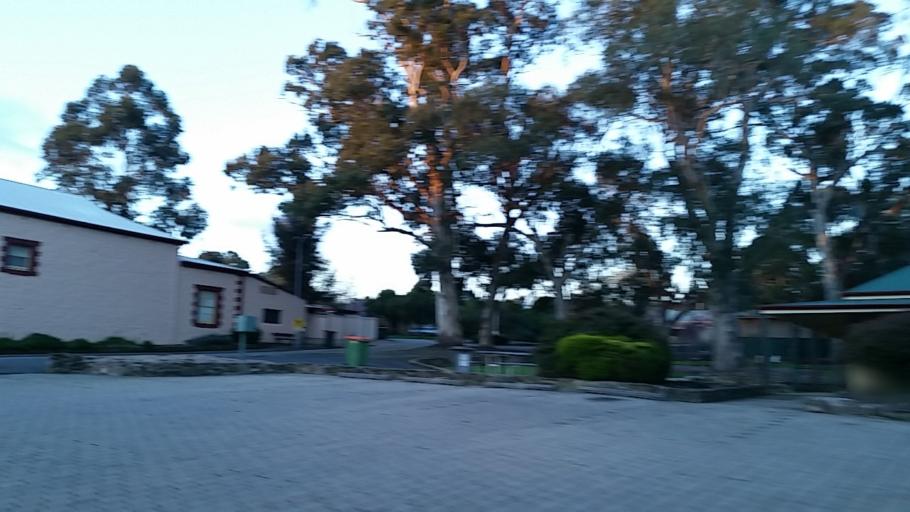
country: AU
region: South Australia
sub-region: Barossa
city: Williamstown
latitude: -34.6704
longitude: 138.8904
